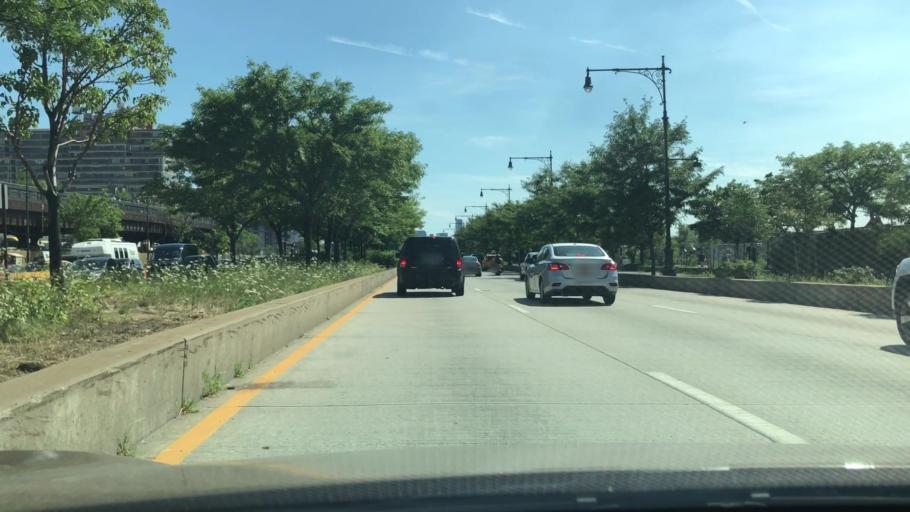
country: US
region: New Jersey
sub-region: Hudson County
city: Weehawken
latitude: 40.7565
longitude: -74.0054
